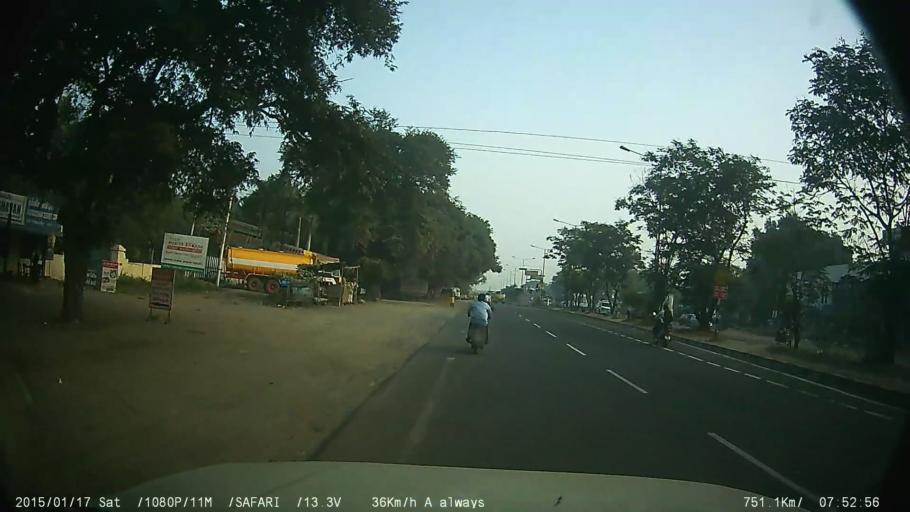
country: IN
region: Tamil Nadu
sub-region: Kancheepuram
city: Vandalur
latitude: 12.8780
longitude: 80.0796
